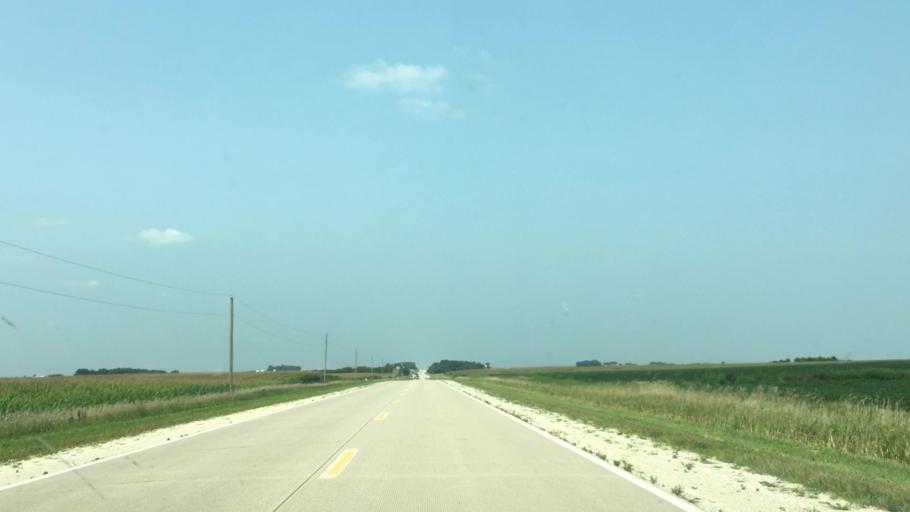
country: US
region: Iowa
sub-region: Fayette County
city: Fayette
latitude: 42.7483
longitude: -91.8041
